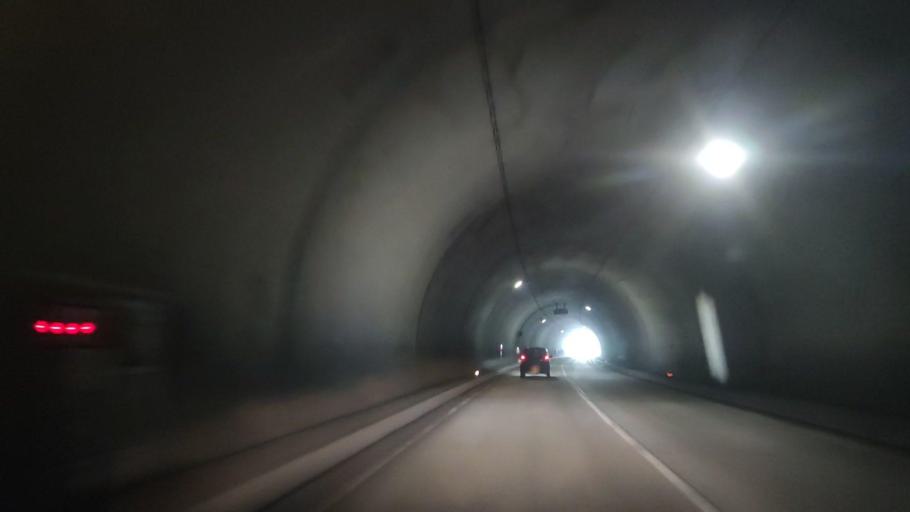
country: JP
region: Tottori
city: Kurayoshi
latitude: 35.4151
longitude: 133.8517
